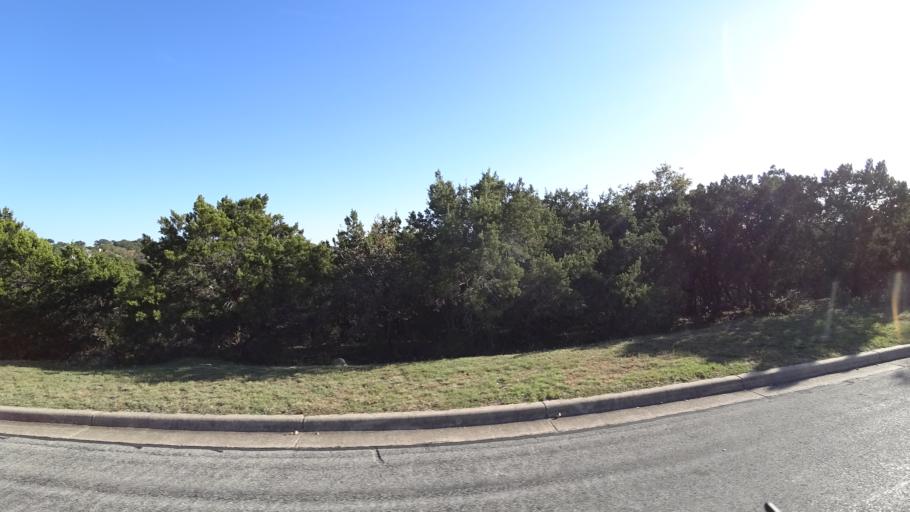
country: US
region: Texas
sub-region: Williamson County
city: Jollyville
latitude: 30.4092
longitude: -97.7739
